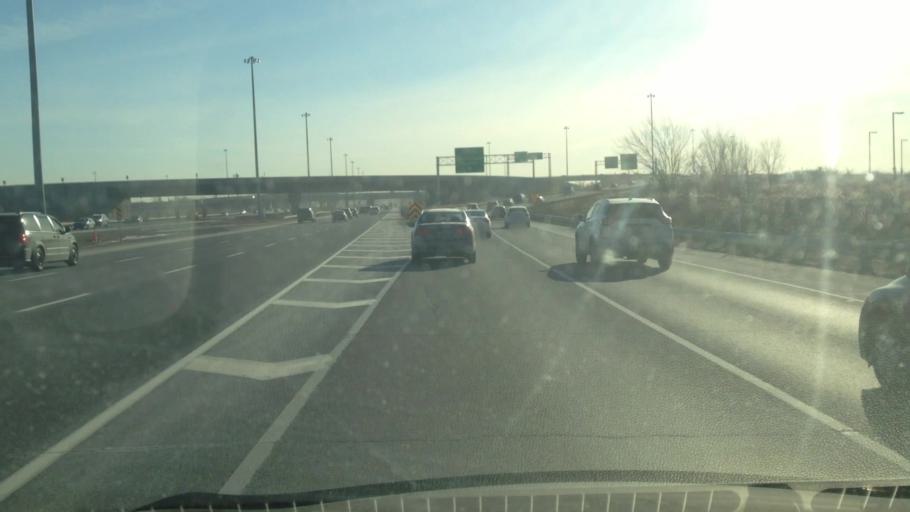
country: CA
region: Quebec
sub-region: Laurentides
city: Boisbriand
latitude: 45.6308
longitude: -73.8459
